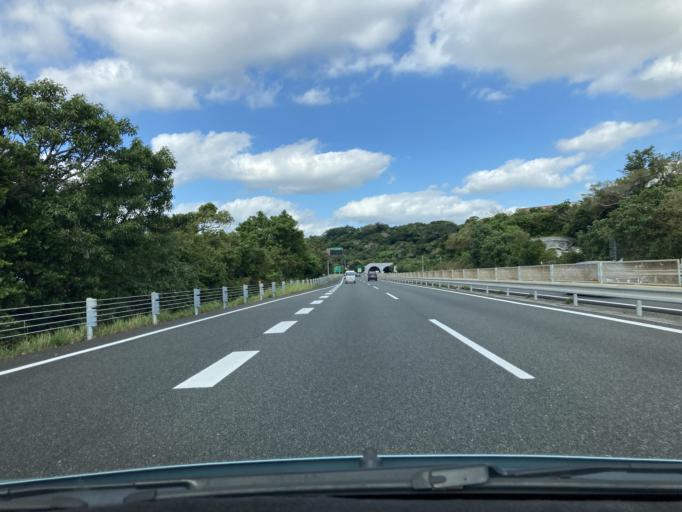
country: JP
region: Okinawa
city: Chatan
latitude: 26.3032
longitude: 127.7912
